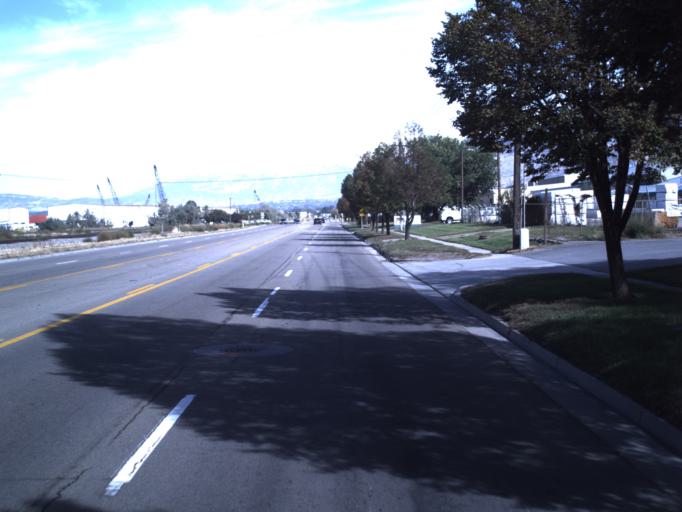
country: US
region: Utah
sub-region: Utah County
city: Lindon
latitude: 40.3346
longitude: -111.7388
